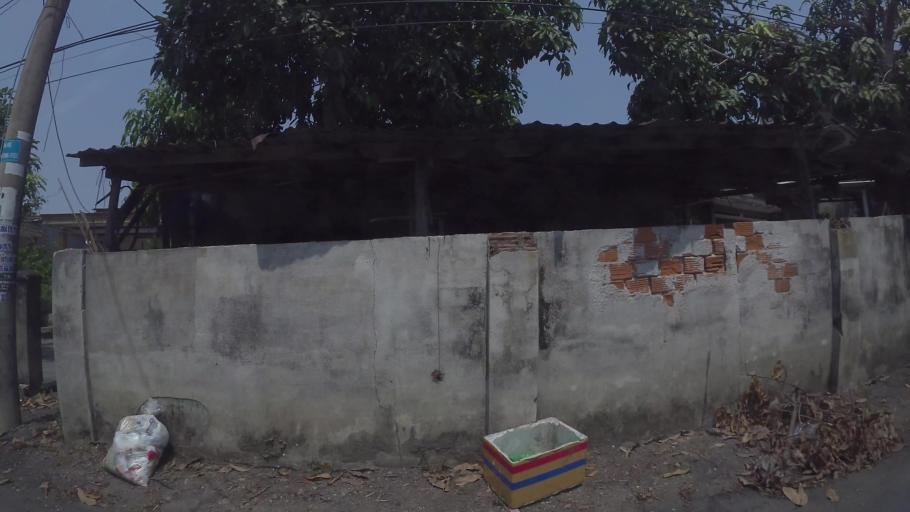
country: VN
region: Da Nang
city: Ngu Hanh Son
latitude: 15.9884
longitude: 108.2549
